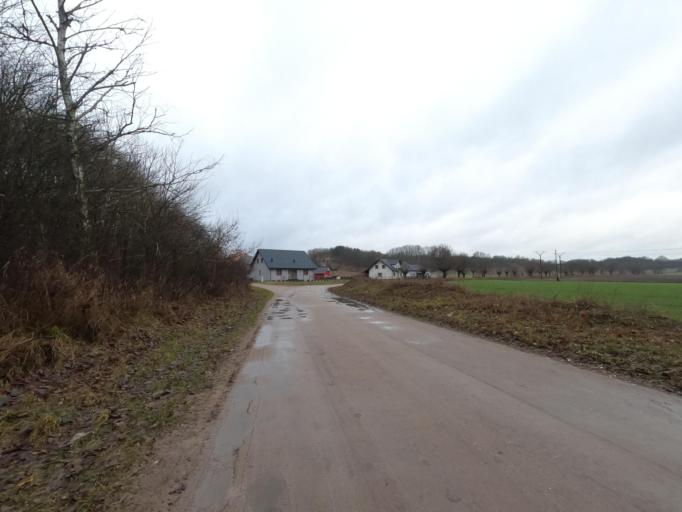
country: PL
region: Greater Poland Voivodeship
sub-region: Powiat pilski
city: Osiek nad Notecia
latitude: 53.1246
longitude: 17.3011
